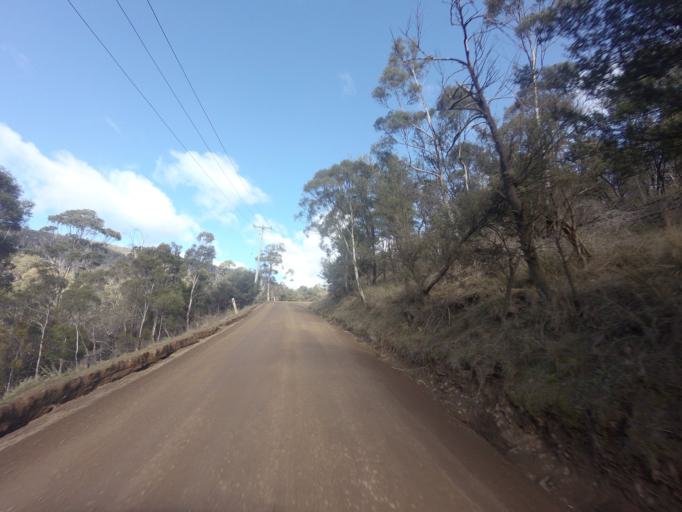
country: AU
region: Tasmania
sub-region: Derwent Valley
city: New Norfolk
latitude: -42.8180
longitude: 147.1278
